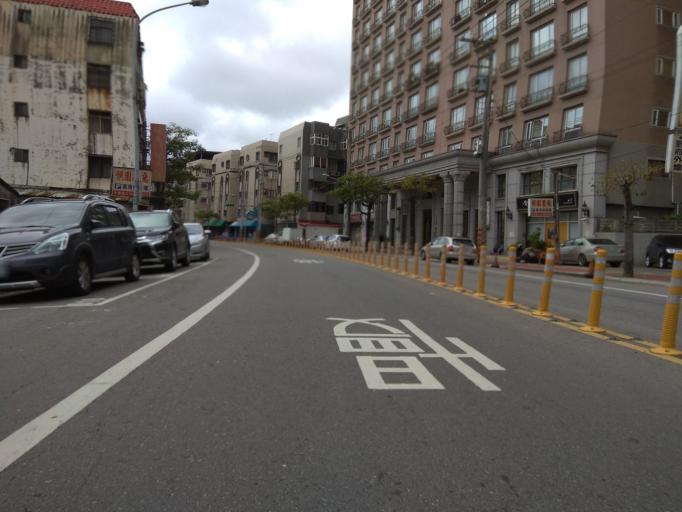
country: TW
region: Taiwan
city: Taoyuan City
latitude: 24.9637
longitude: 121.2134
